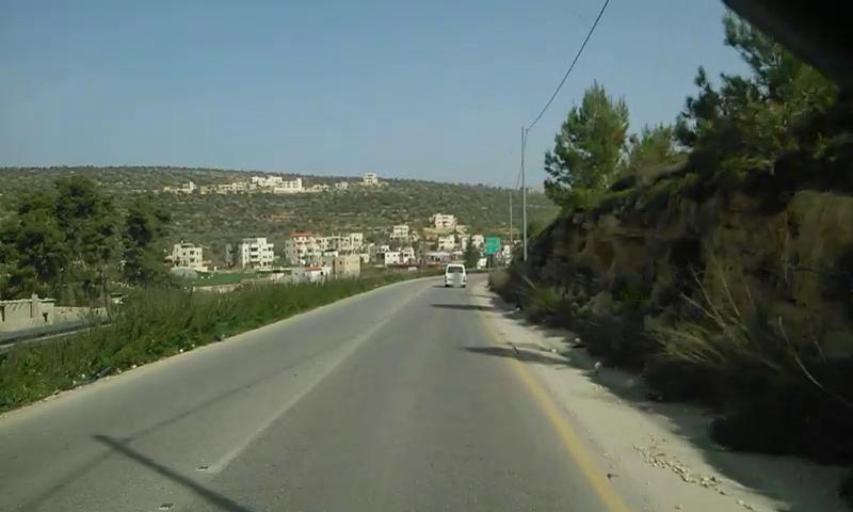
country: PS
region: West Bank
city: Dura al Qar`
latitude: 31.9680
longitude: 35.2274
